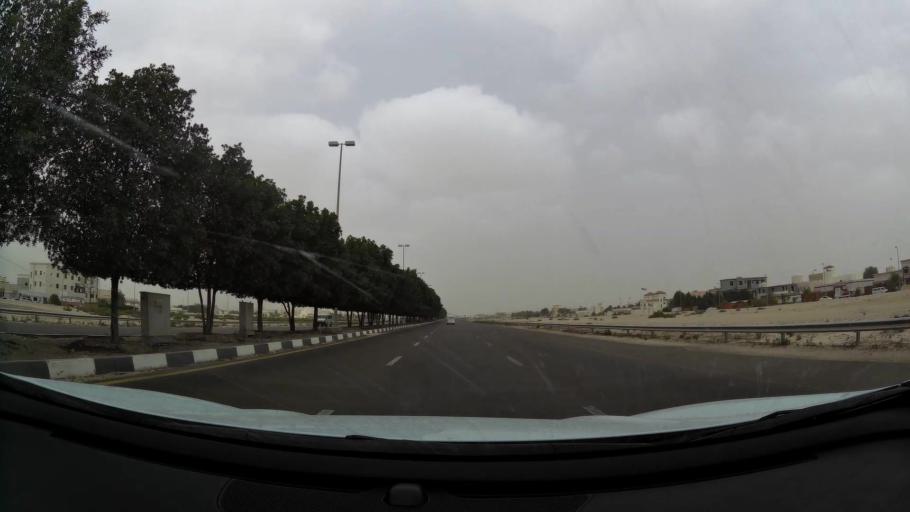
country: AE
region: Abu Dhabi
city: Abu Dhabi
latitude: 24.3933
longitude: 54.7182
